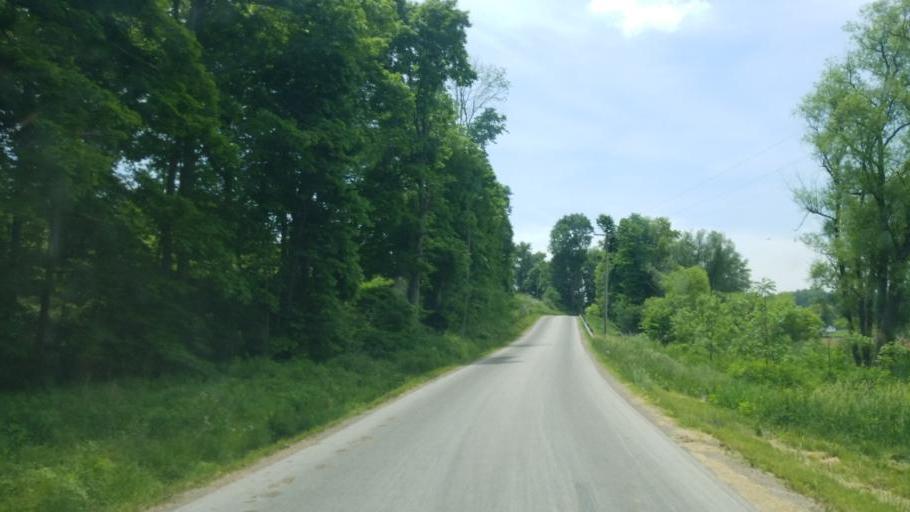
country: US
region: Ohio
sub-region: Coshocton County
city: West Lafayette
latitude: 40.3865
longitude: -81.7523
